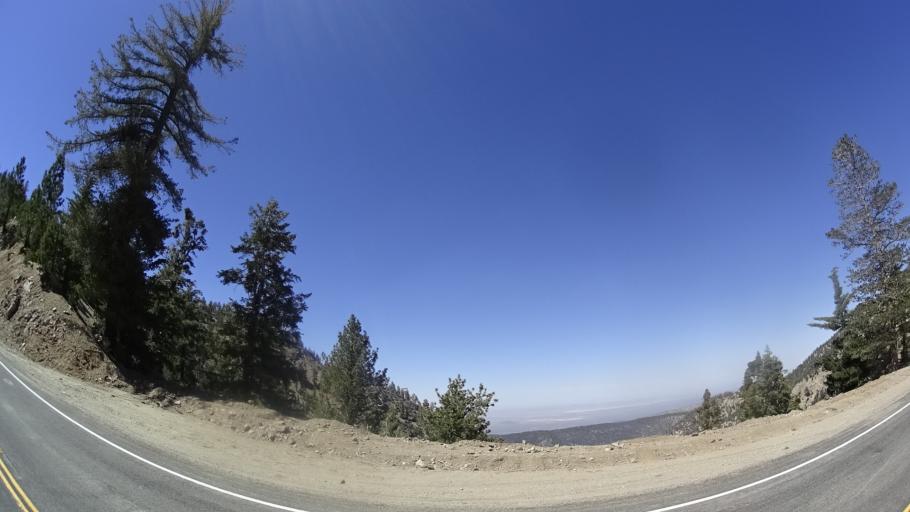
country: US
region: California
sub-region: San Bernardino County
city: Wrightwood
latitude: 34.3614
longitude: -117.8001
